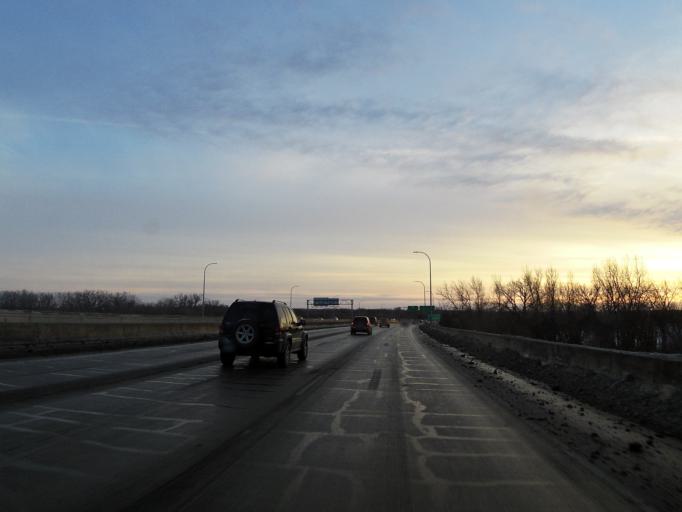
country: US
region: Minnesota
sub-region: Scott County
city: Savage
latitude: 44.7993
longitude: -93.3990
